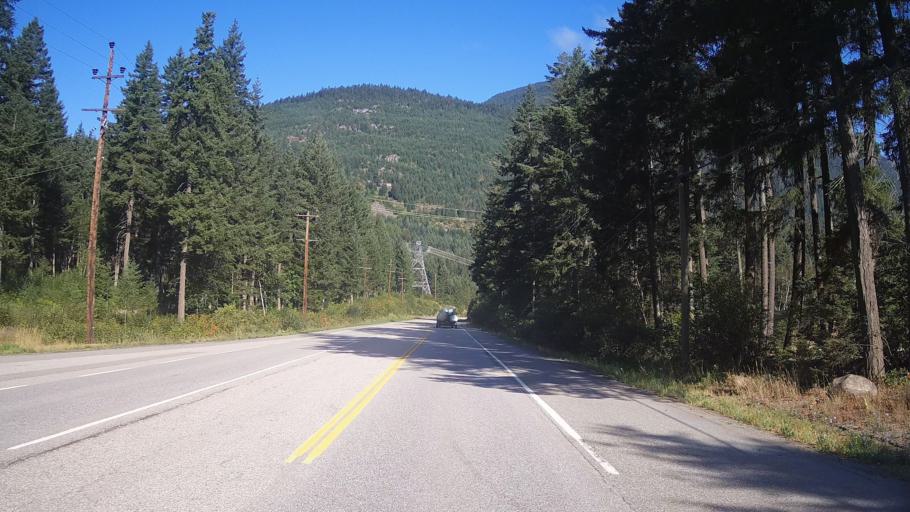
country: CA
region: British Columbia
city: Hope
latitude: 49.6616
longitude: -121.4138
